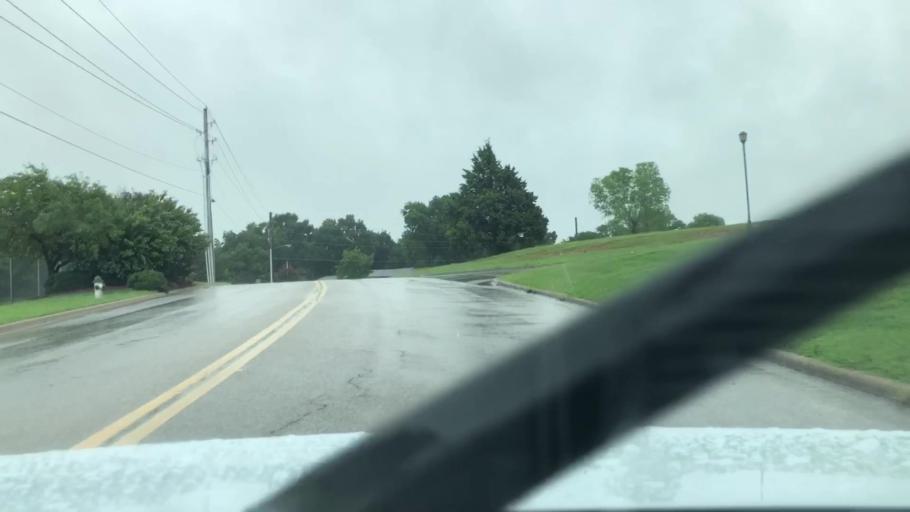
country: US
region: Oklahoma
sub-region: Washington County
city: Bartlesville
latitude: 36.7389
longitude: -95.9321
